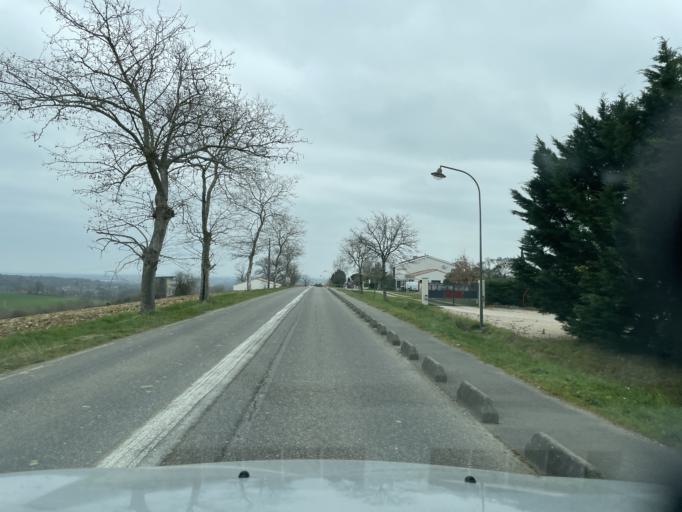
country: FR
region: Midi-Pyrenees
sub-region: Departement du Gers
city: Pujaudran
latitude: 43.5895
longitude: 1.1554
